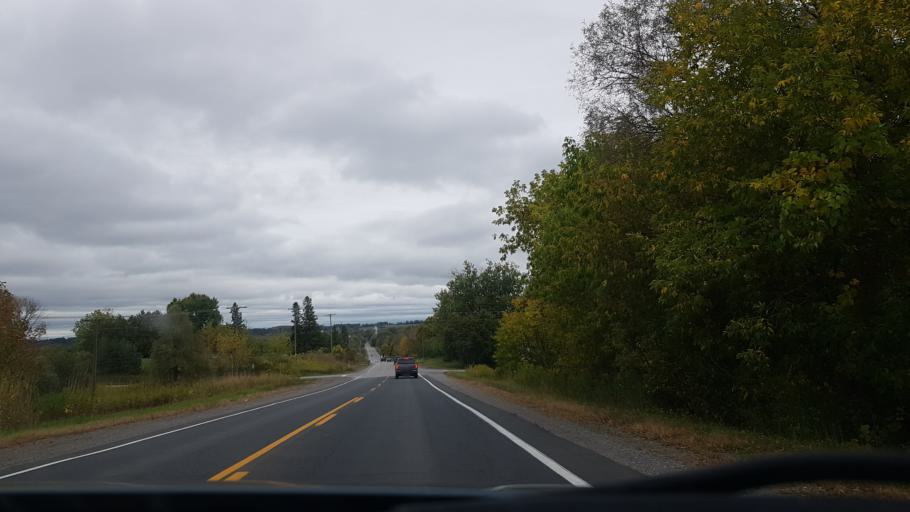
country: CA
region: Ontario
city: Omemee
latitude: 44.2125
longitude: -78.4743
